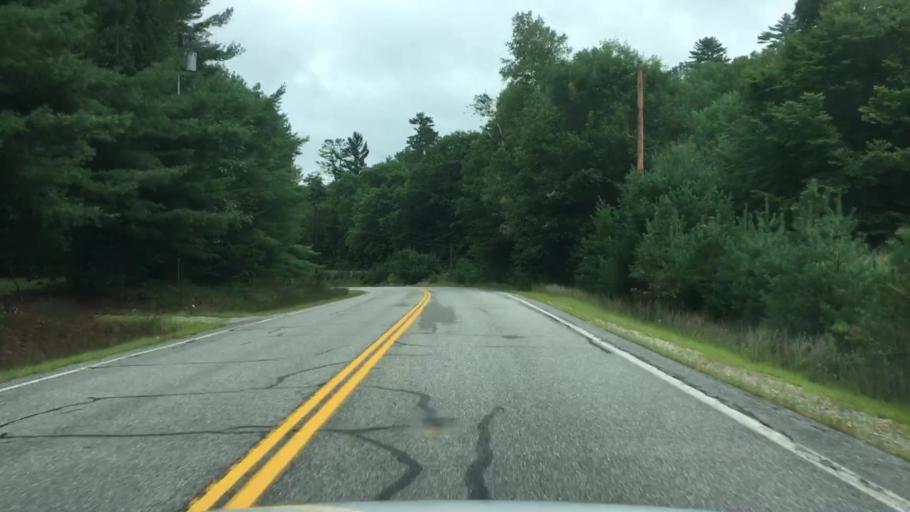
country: US
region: Maine
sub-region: Oxford County
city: Hiram
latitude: 43.8922
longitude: -70.8224
